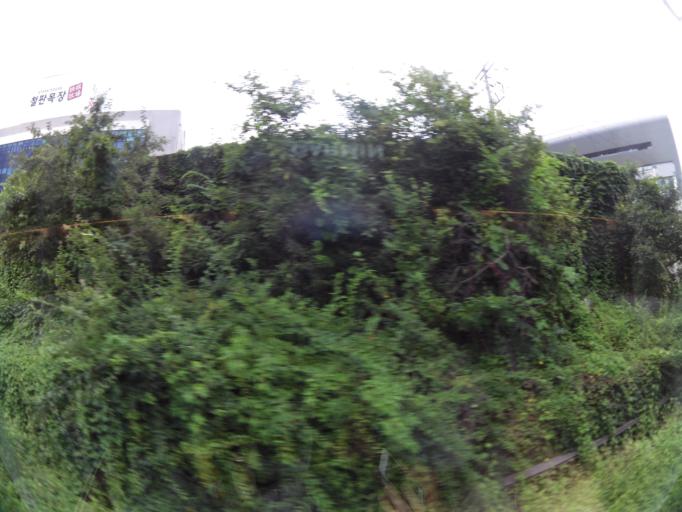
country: KR
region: Seoul
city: Seoul
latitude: 37.5144
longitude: 126.9354
